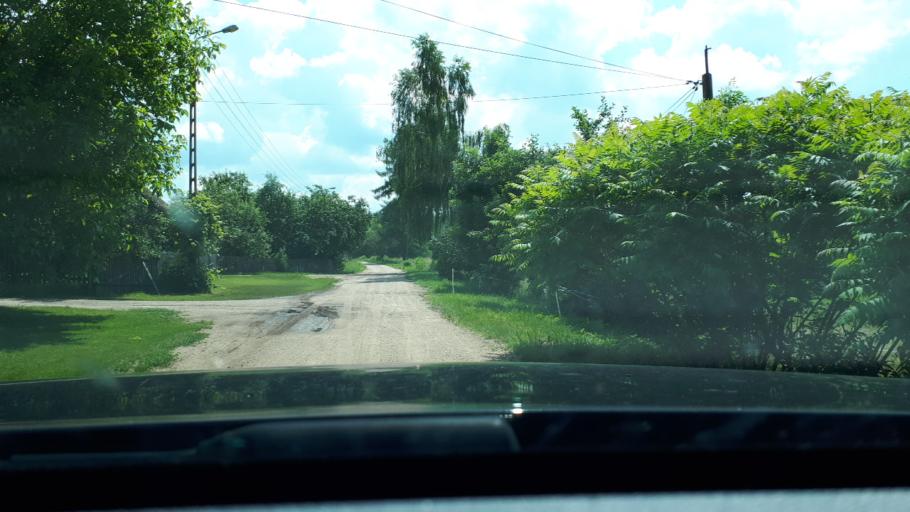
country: PL
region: Podlasie
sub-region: Powiat bialostocki
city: Suprasl
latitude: 53.2443
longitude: 23.3507
